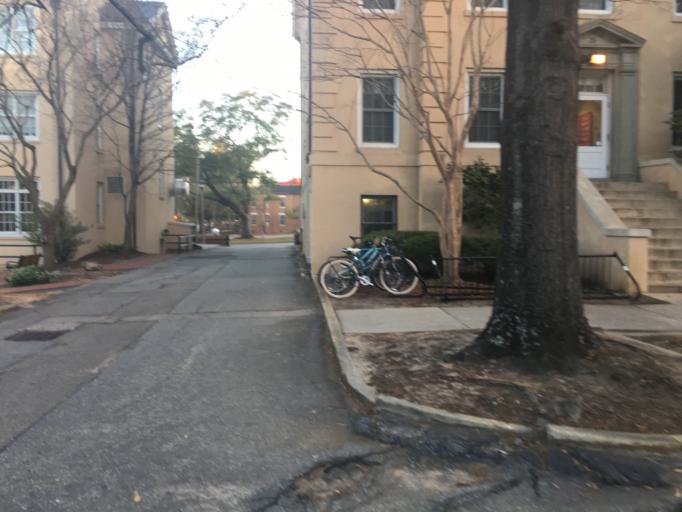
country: US
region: South Carolina
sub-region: Richland County
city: Columbia
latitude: 33.9991
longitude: -81.0286
